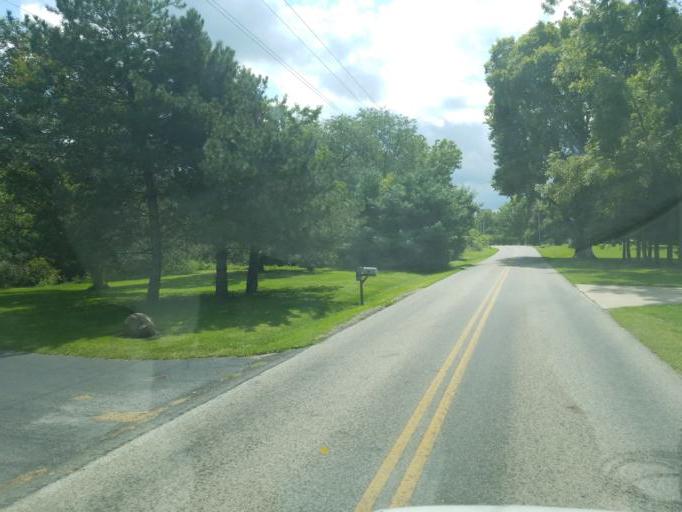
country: US
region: Ohio
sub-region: Huron County
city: Norwalk
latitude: 41.1545
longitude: -82.6344
